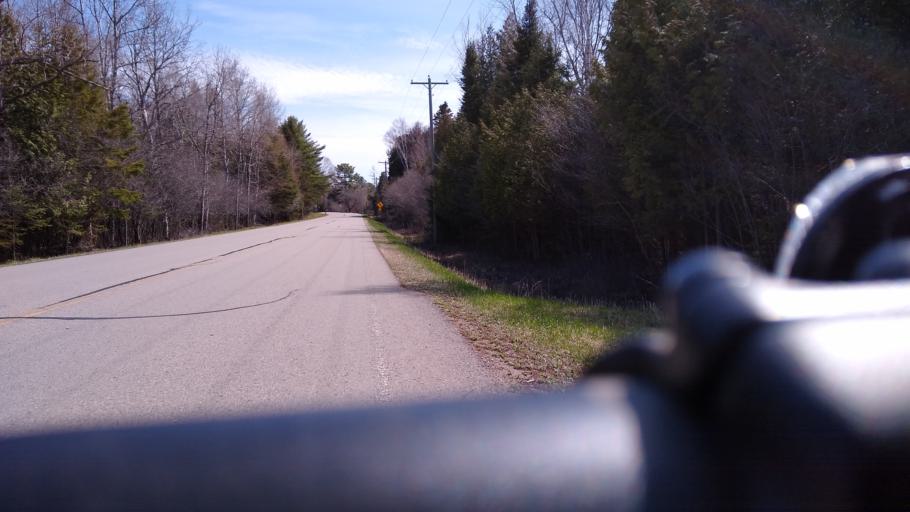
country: US
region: Michigan
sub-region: Delta County
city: Escanaba
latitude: 45.6901
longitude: -87.1526
